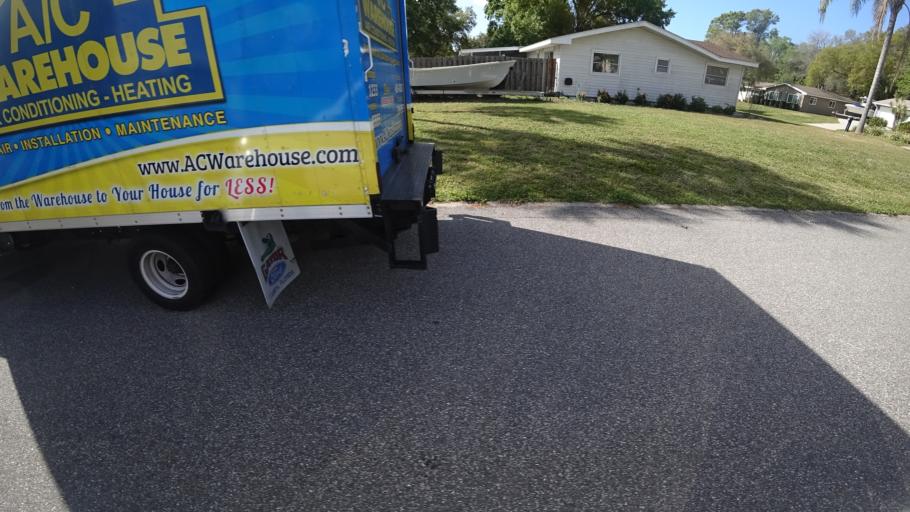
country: US
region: Florida
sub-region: Manatee County
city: Whitfield
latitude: 27.4235
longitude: -82.5584
